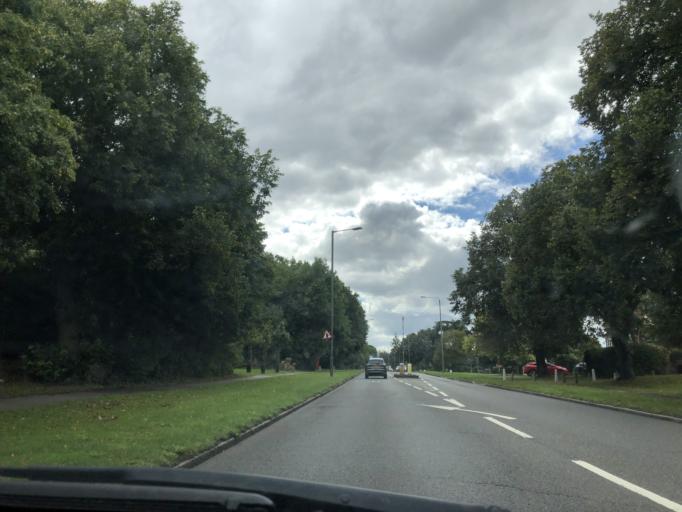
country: GB
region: England
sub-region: Greater London
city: Orpington
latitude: 51.3687
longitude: 0.1097
